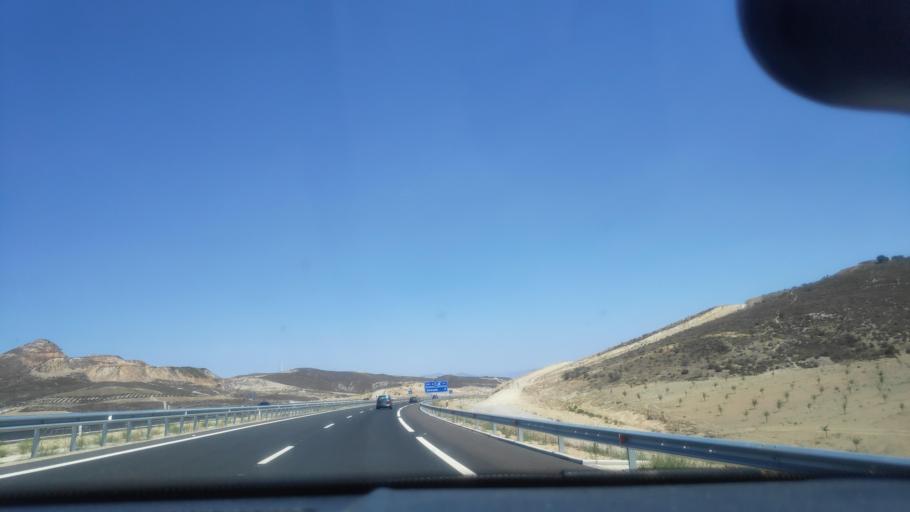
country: ES
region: Andalusia
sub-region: Provincia de Granada
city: Alhendin
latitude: 37.0919
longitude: -3.6721
